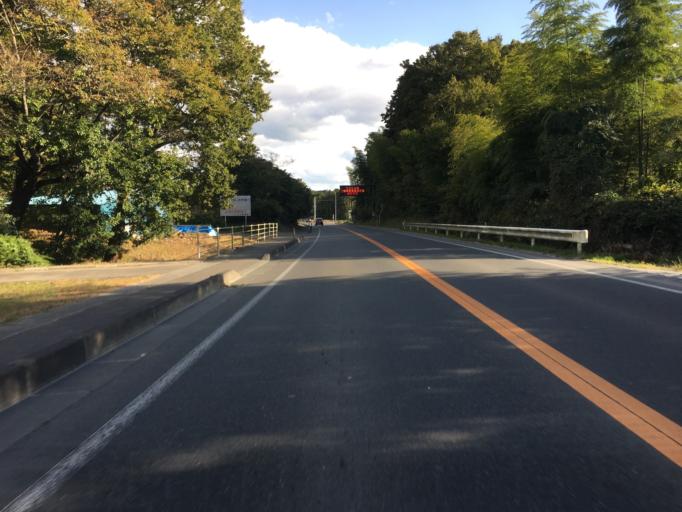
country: JP
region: Miyagi
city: Marumori
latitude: 37.8963
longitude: 140.9026
